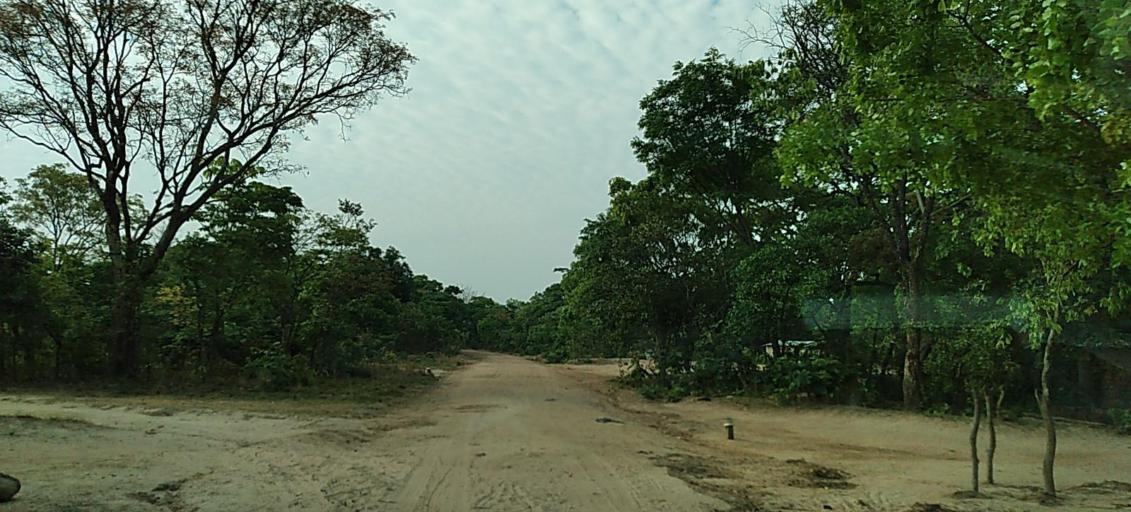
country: ZM
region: Copperbelt
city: Kalulushi
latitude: -12.9011
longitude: 27.6862
